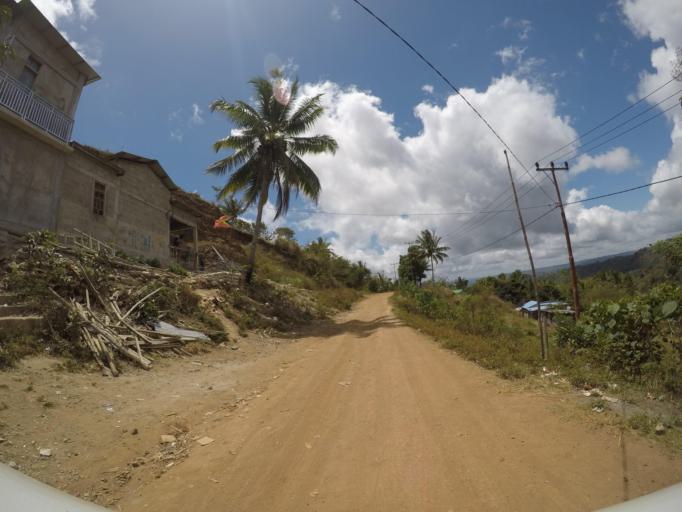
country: TL
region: Lautem
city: Lospalos
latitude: -8.5519
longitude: 126.8291
